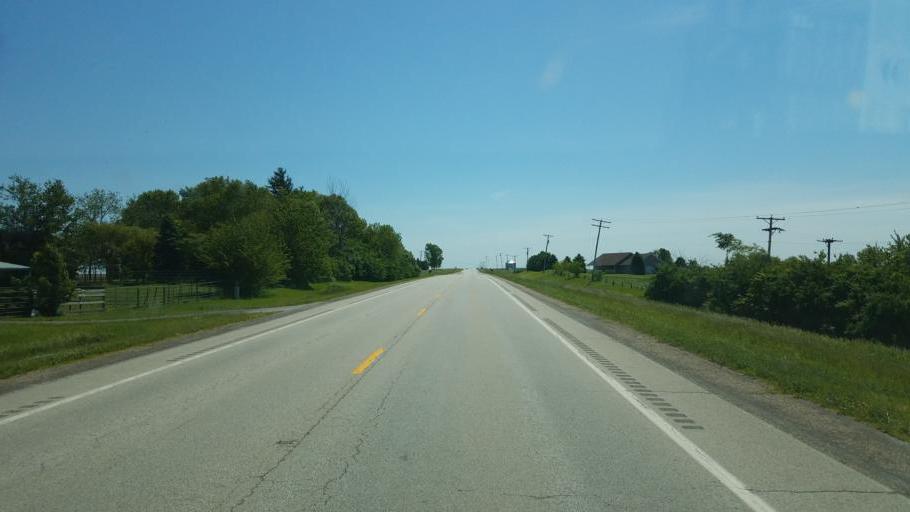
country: US
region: Illinois
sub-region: McLean County
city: Heyworth
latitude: 40.3122
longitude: -88.9503
